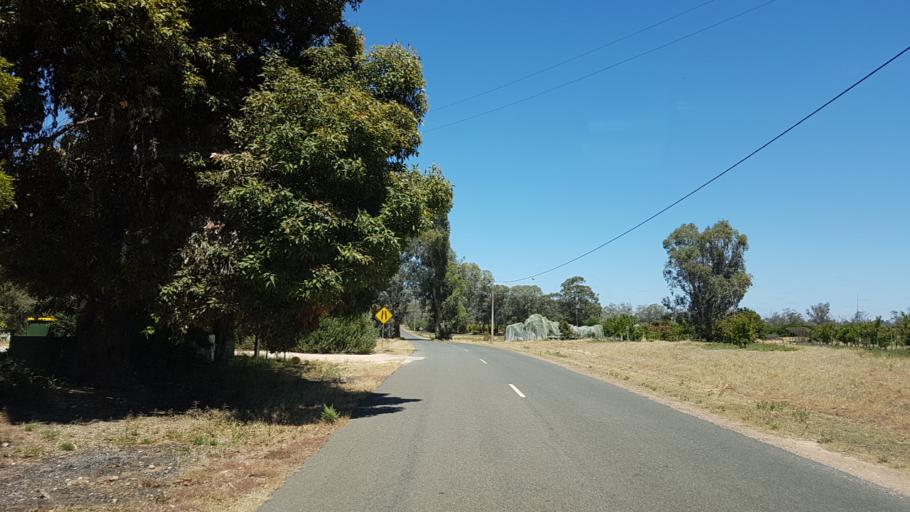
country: AU
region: South Australia
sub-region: Loxton Waikerie
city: Waikerie
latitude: -34.1650
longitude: 140.0296
